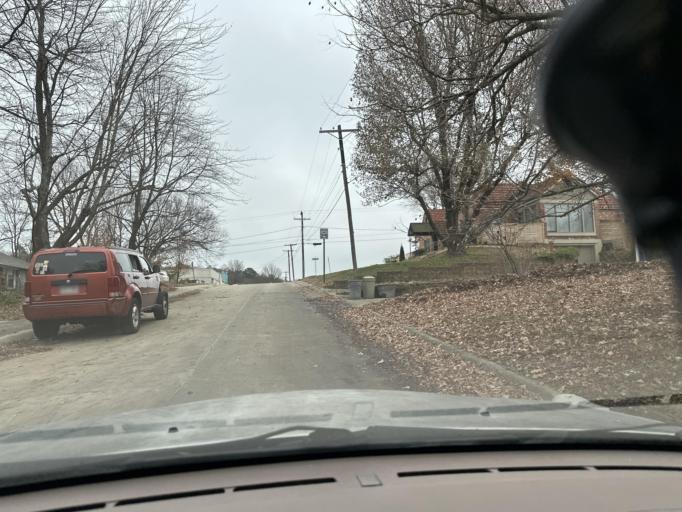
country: US
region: Arkansas
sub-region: Washington County
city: Fayetteville
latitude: 36.0753
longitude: -94.1585
